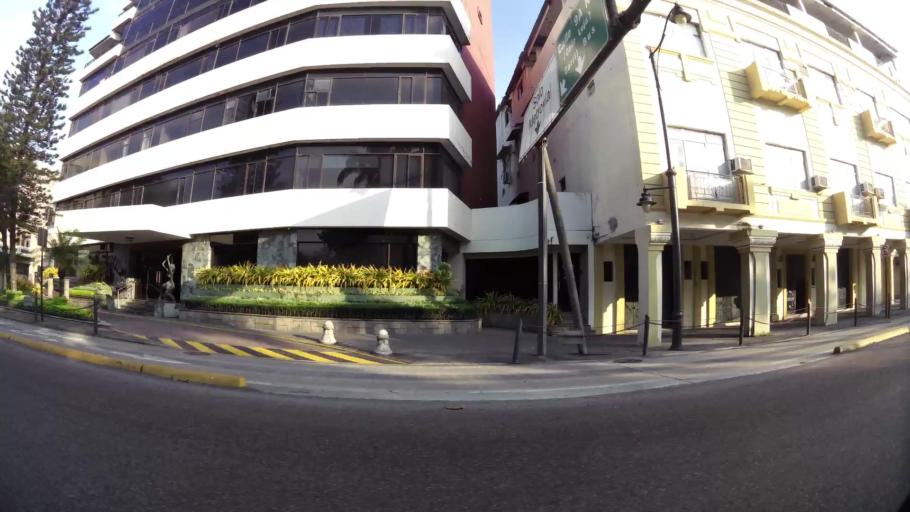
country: EC
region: Guayas
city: Eloy Alfaro
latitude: -2.1865
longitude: -79.8773
